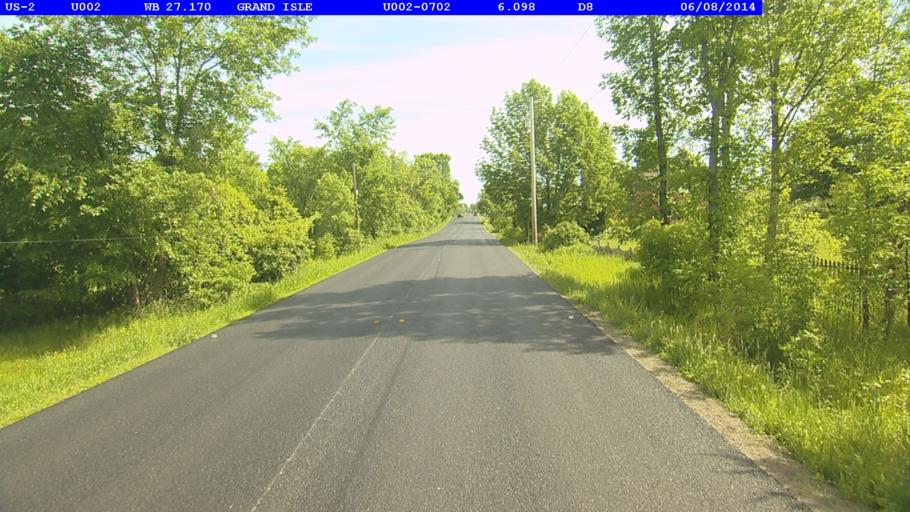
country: US
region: New York
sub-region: Clinton County
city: Cumberland Head
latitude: 44.6824
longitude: -73.3143
